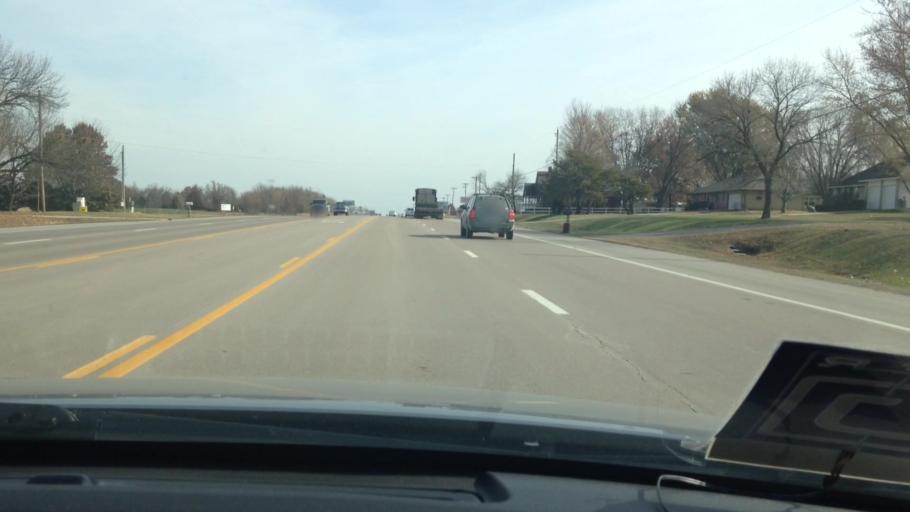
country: US
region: Missouri
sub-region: Henry County
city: Clinton
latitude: 38.3895
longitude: -93.8062
